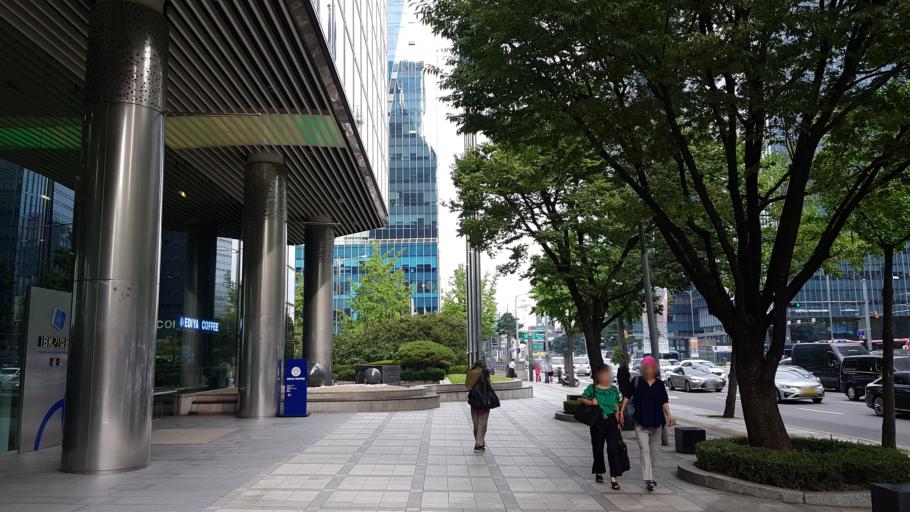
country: KR
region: Seoul
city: Seoul
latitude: 37.5659
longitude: 126.9863
